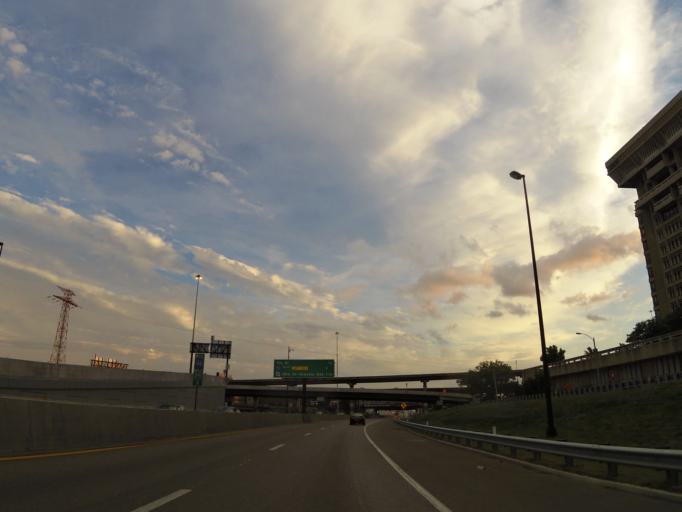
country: US
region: Missouri
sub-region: City of Saint Louis
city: St. Louis
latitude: 38.6220
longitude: -90.1886
